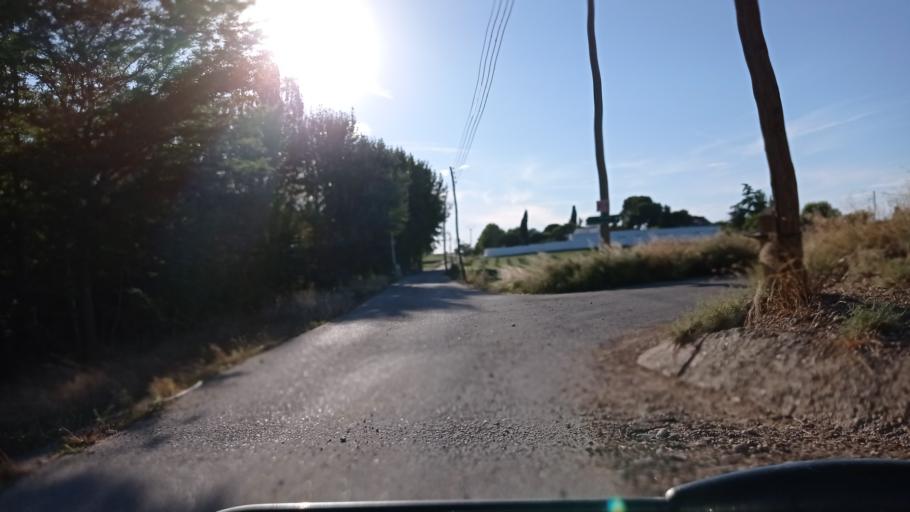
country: ES
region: Aragon
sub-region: Provincia de Zaragoza
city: Oliver-Valdefierro, Oliver, Valdefierro
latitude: 41.6649
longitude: -0.9586
